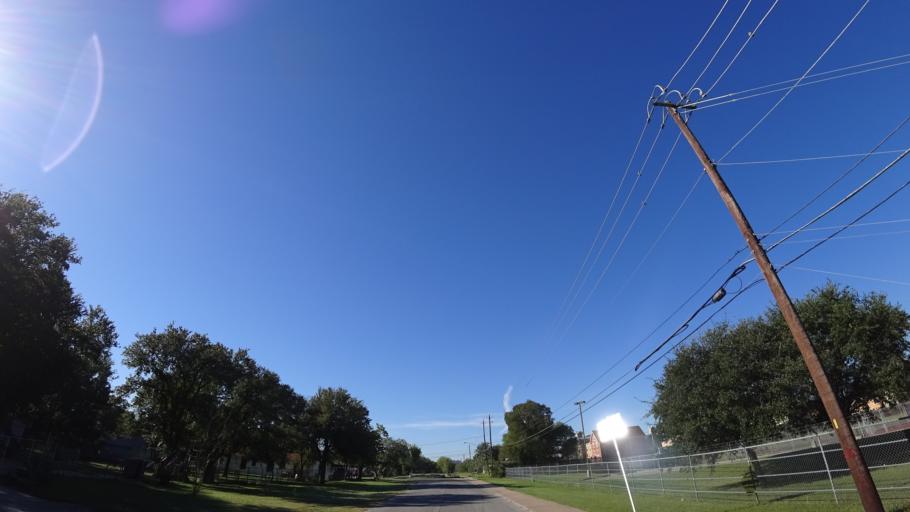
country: US
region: Texas
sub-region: Travis County
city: Austin
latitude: 30.2363
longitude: -97.7015
